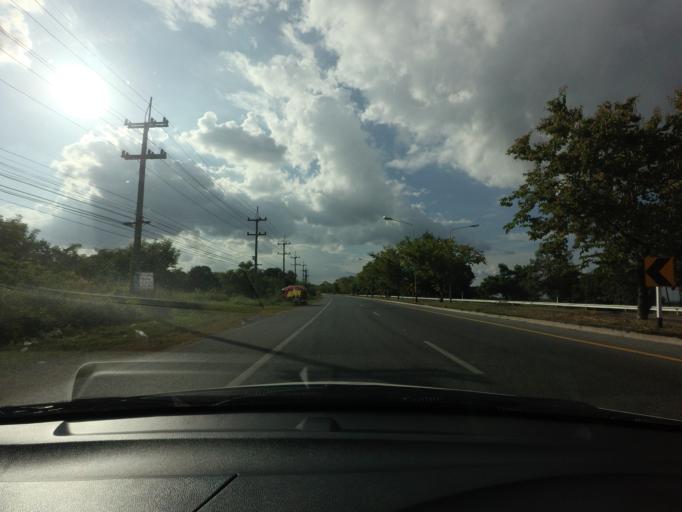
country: TH
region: Nakhon Nayok
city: Nakhon Nayok
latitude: 14.2225
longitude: 101.1461
